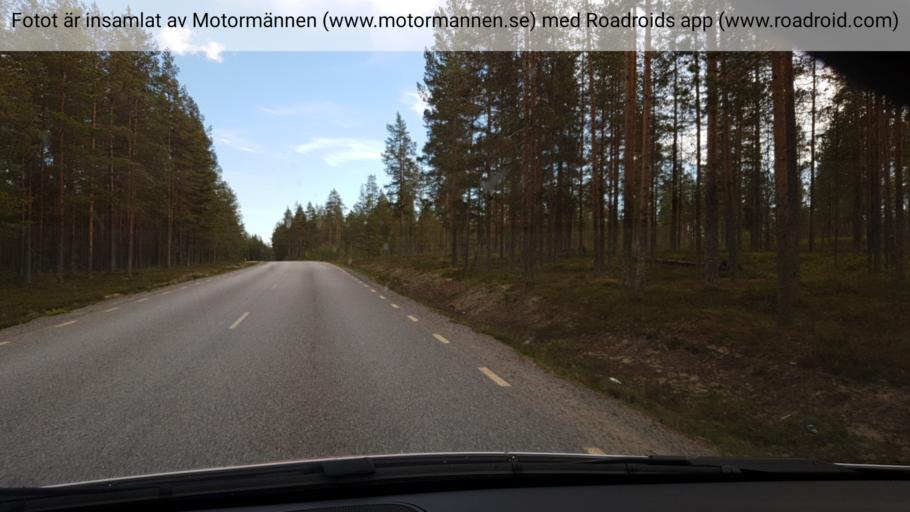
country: SE
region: Vaesterbotten
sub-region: Umea Kommun
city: Saevar
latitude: 63.9912
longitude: 20.4975
